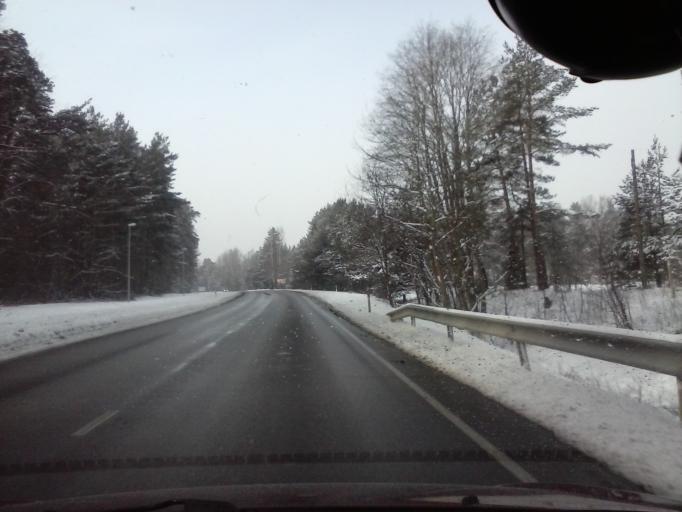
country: EE
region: Paernumaa
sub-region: Paikuse vald
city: Paikuse
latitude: 58.3766
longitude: 24.5658
